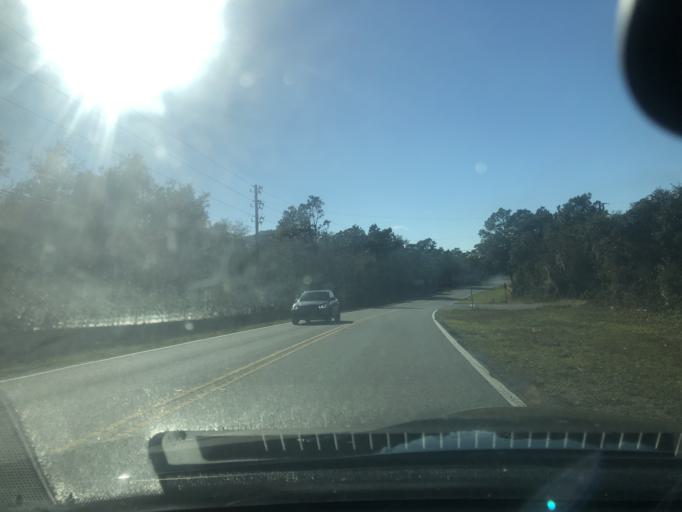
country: US
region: Florida
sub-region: Citrus County
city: Homosassa Springs
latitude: 28.8192
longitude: -82.5341
